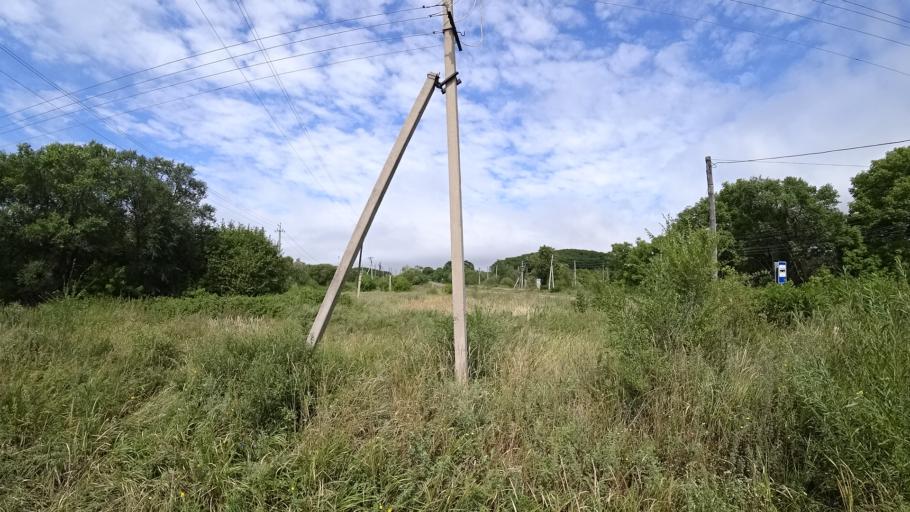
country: RU
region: Primorskiy
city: Lyalichi
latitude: 44.1380
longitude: 132.3876
